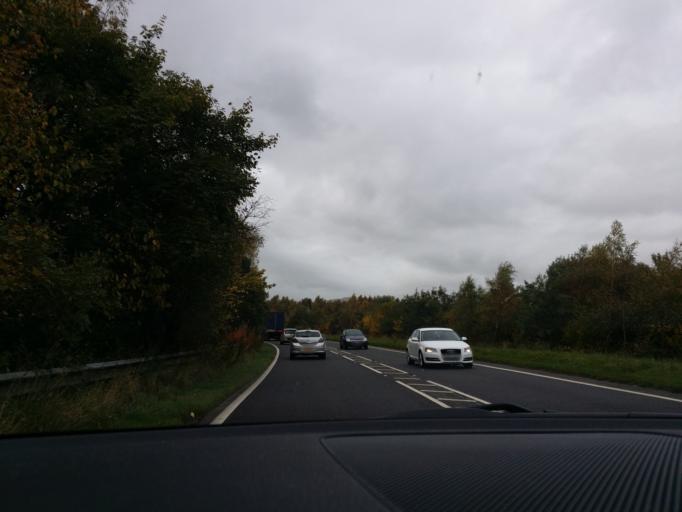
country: GB
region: Scotland
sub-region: Clackmannanshire
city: Clackmannan
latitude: 56.1120
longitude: -3.7454
